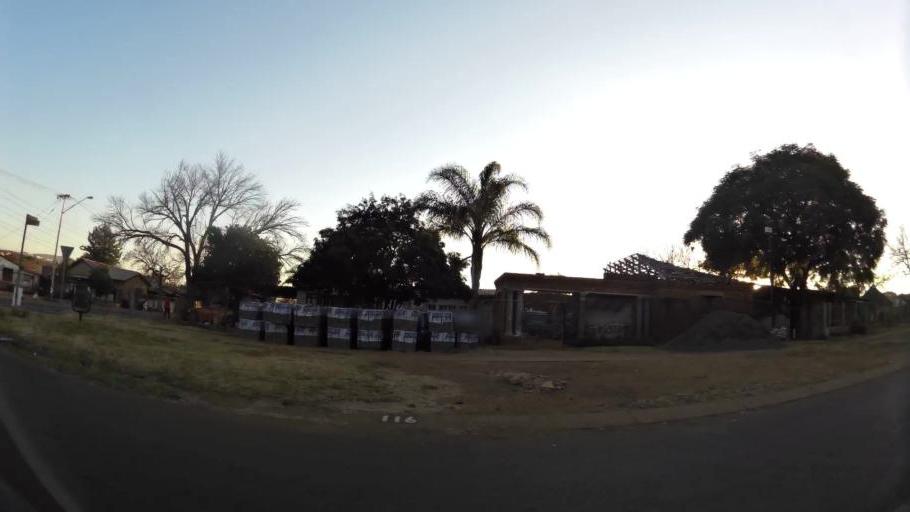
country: ZA
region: Gauteng
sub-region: City of Tshwane Metropolitan Municipality
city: Pretoria
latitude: -25.7462
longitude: 28.1260
